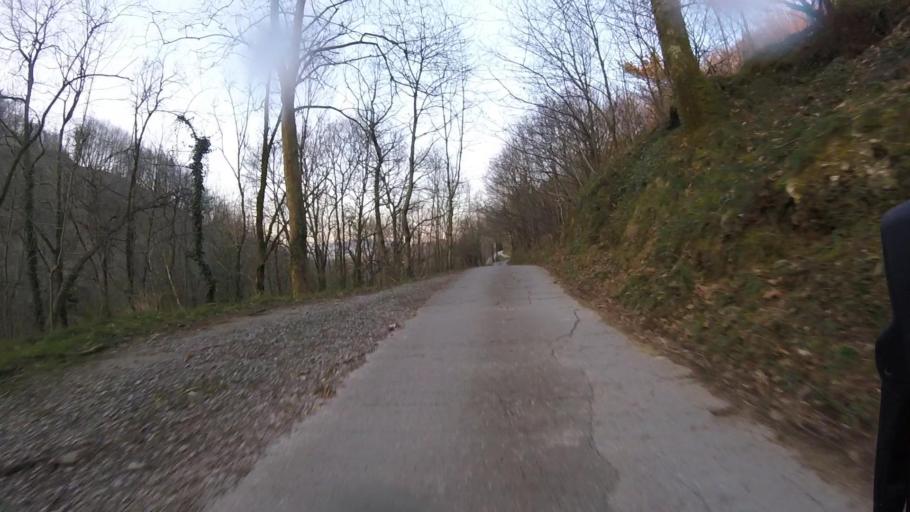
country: ES
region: Basque Country
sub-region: Provincia de Guipuzcoa
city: Errenteria
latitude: 43.2819
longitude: -1.8719
